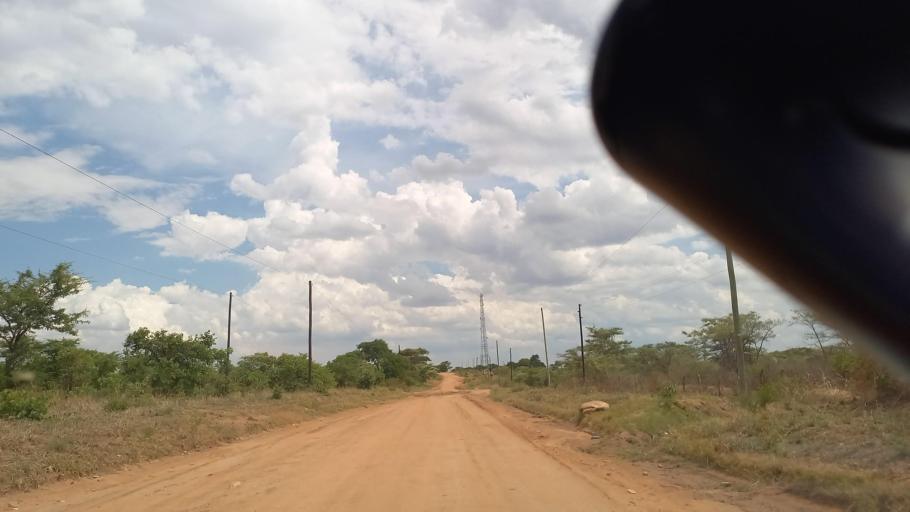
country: ZM
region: Southern
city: Nakambala
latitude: -16.0316
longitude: 27.9689
